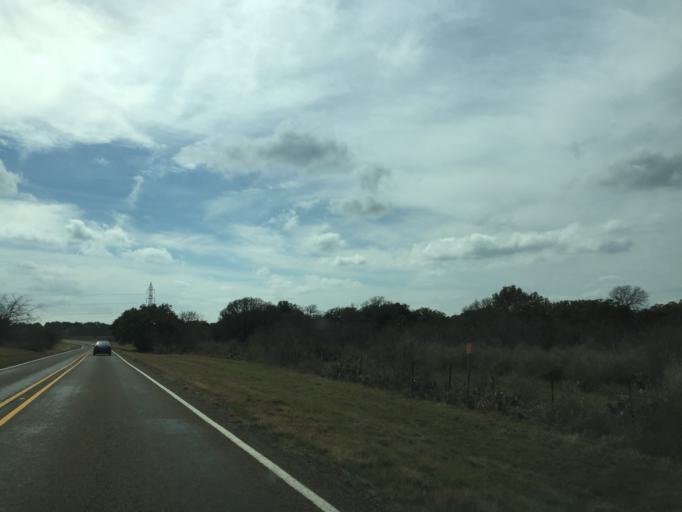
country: US
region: Texas
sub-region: Burnet County
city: Granite Shoals
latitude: 30.5269
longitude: -98.4468
